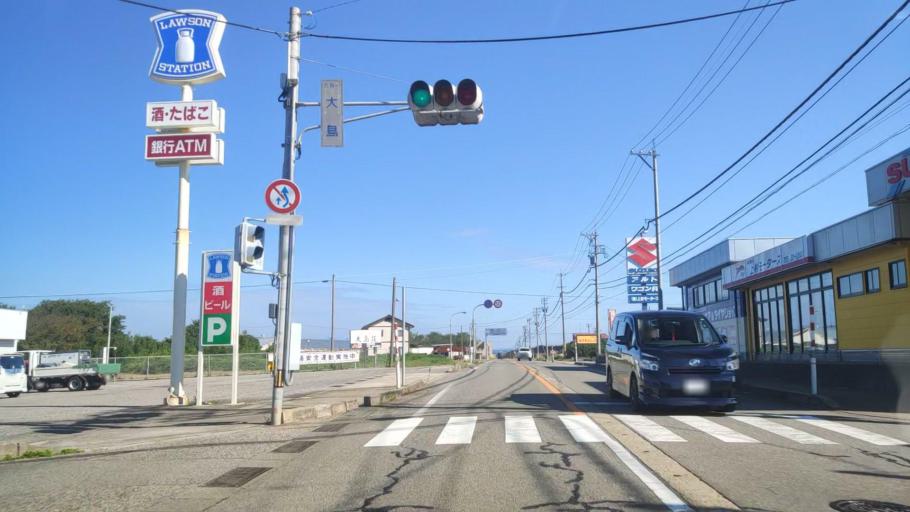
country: JP
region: Ishikawa
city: Hakui
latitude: 36.9880
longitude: 136.7760
